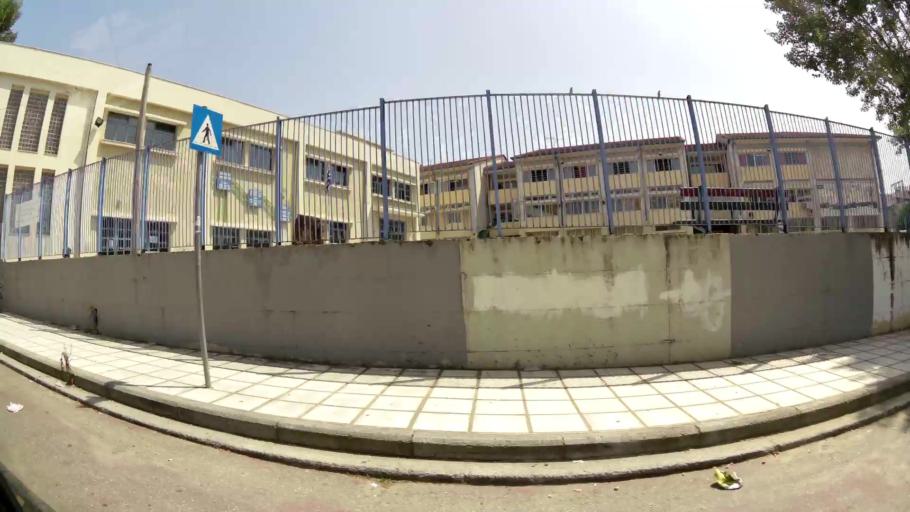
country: GR
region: Central Macedonia
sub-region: Nomos Thessalonikis
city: Evosmos
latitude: 40.6754
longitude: 22.9028
